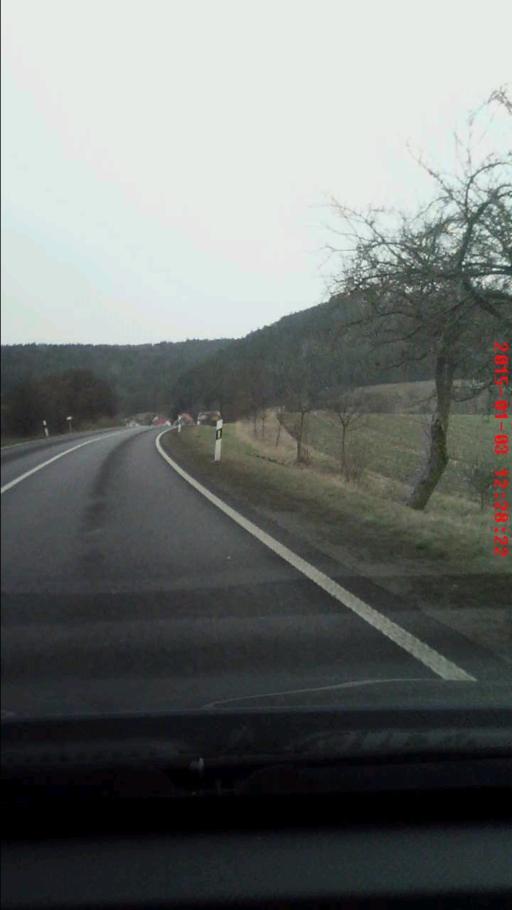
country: DE
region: Thuringia
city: Nauendorf
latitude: 50.8882
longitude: 11.1799
